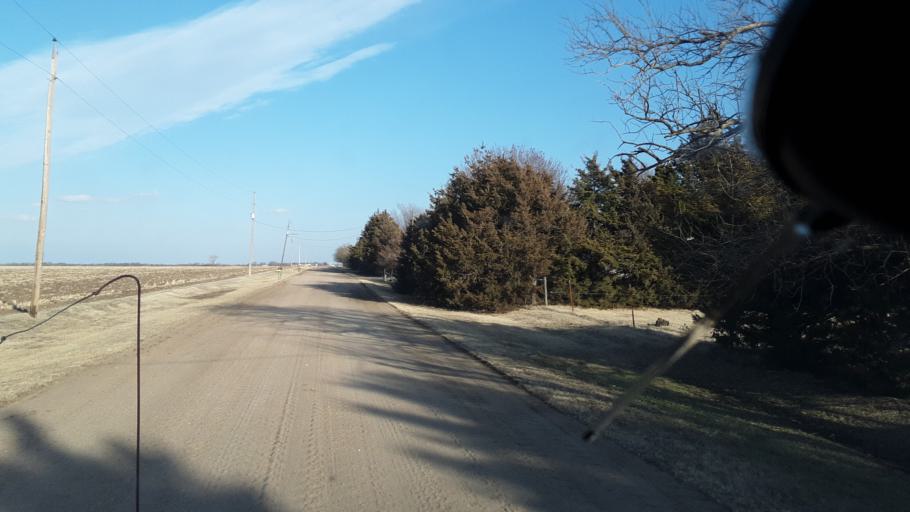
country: US
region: Kansas
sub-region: Reno County
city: South Hutchinson
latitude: 37.9842
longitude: -97.9727
